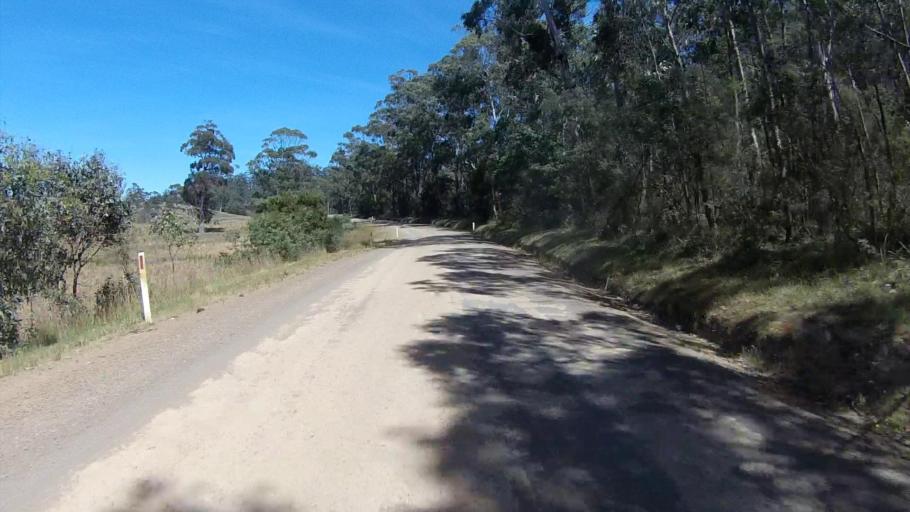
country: AU
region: Tasmania
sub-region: Sorell
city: Sorell
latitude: -42.7531
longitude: 147.6899
